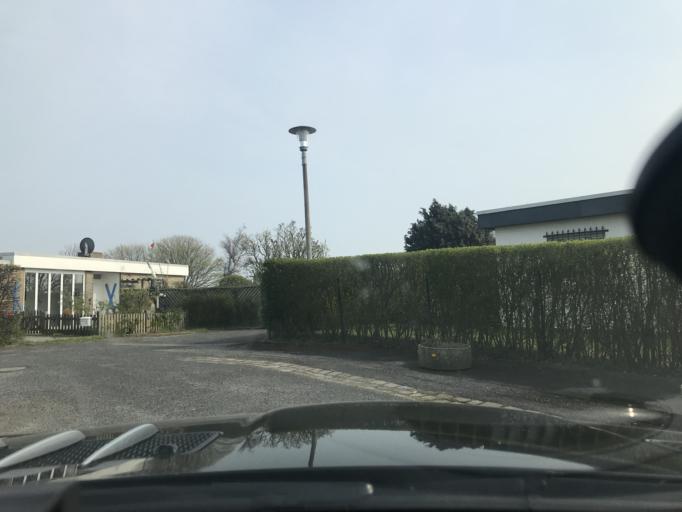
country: DE
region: Schleswig-Holstein
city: Burg auf Fehmarn
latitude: 54.4906
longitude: 11.2415
